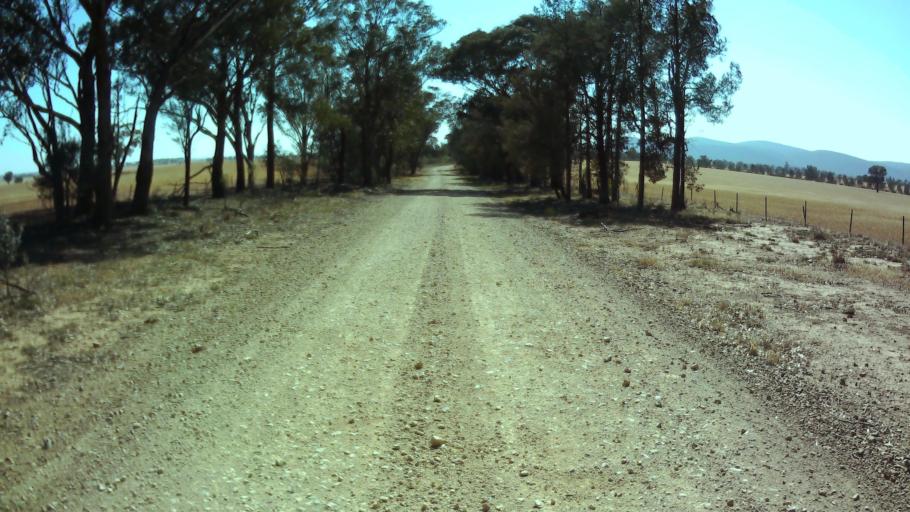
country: AU
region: New South Wales
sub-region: Weddin
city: Grenfell
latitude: -33.9052
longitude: 147.8568
